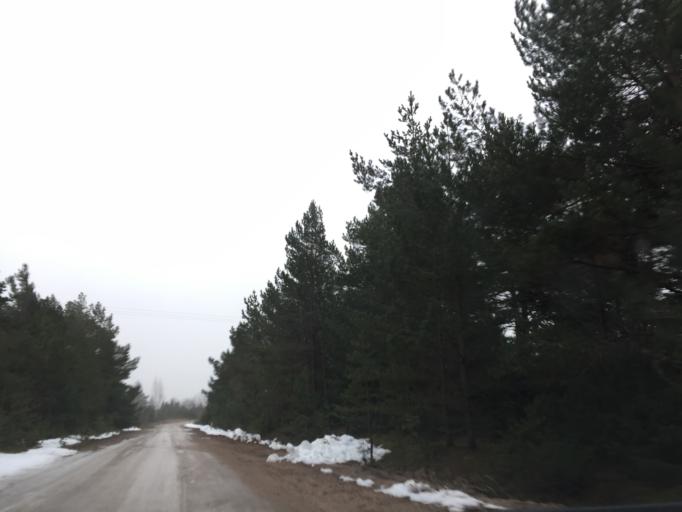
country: EE
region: Saare
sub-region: Kuressaare linn
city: Kuressaare
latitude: 58.4954
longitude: 21.9836
